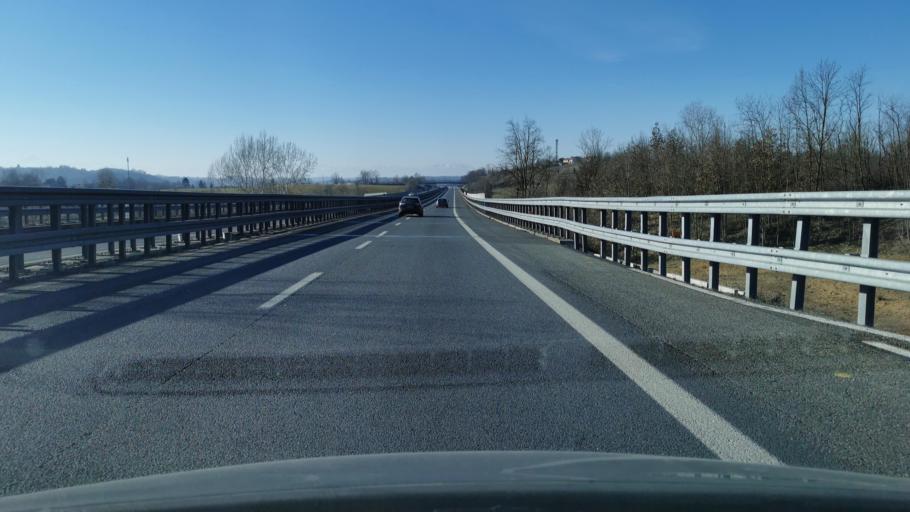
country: IT
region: Piedmont
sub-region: Provincia di Asti
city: Baldichieri d'Asti
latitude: 44.9019
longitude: 8.1217
